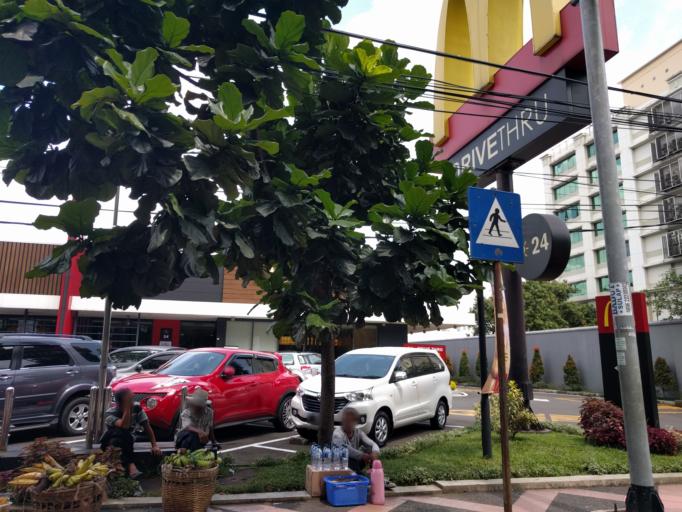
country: ID
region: West Java
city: Bogor
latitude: -6.6011
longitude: 106.7950
